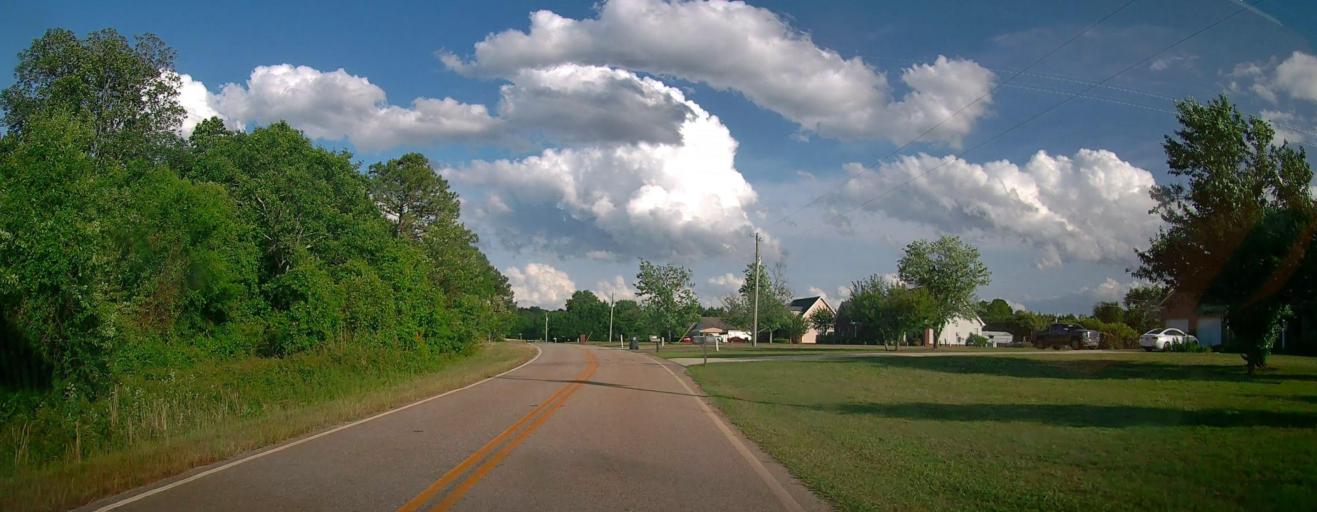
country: US
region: Georgia
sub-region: Peach County
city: Byron
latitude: 32.6625
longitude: -83.7977
